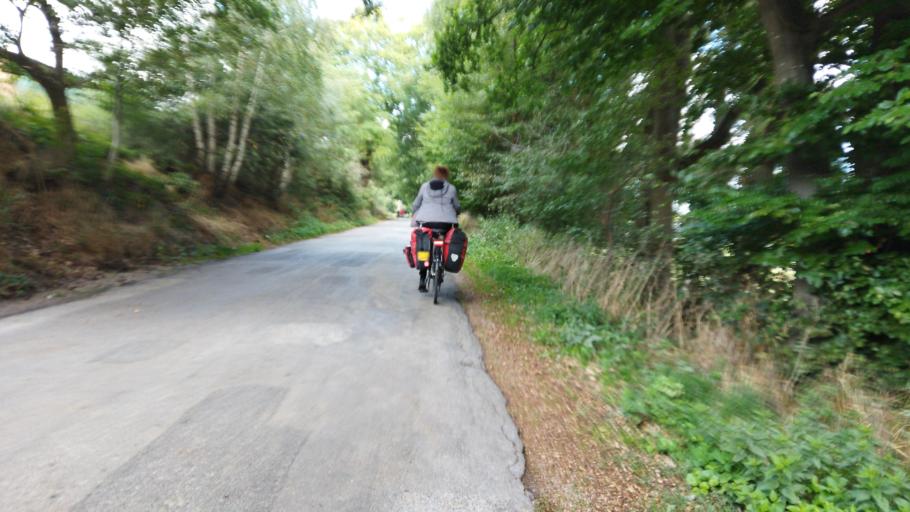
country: DE
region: Lower Saxony
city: Emsburen
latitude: 52.3802
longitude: 7.3323
